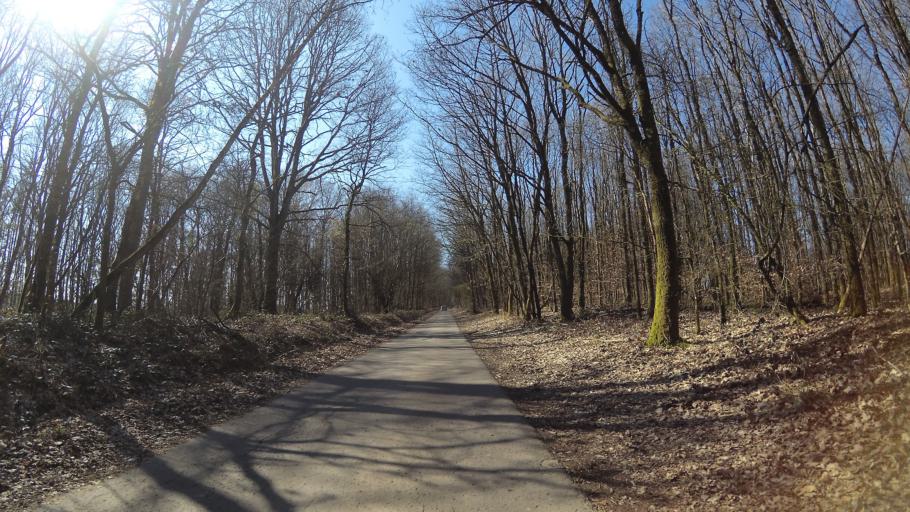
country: DE
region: Saarland
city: Marpingen
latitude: 49.4380
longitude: 7.0123
